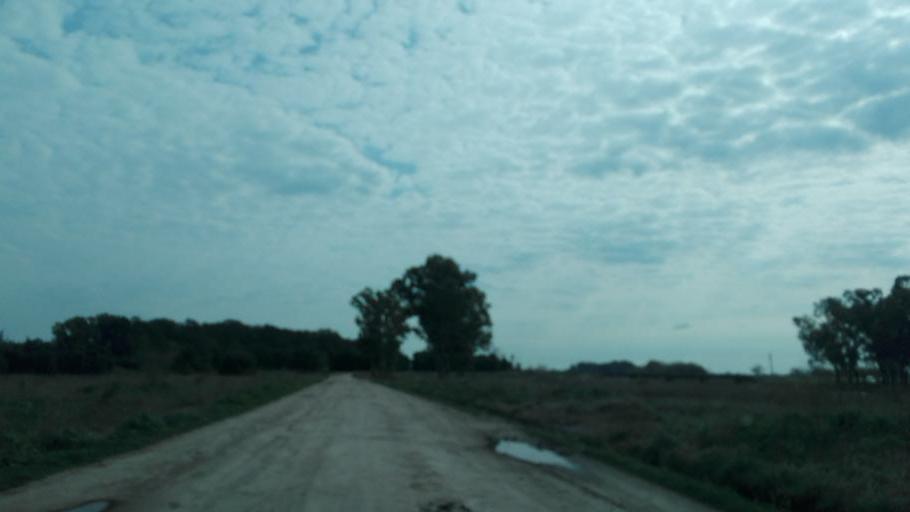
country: AR
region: Buenos Aires
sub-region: Partido de Chascomus
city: Chascomus
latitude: -35.5428
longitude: -58.0740
